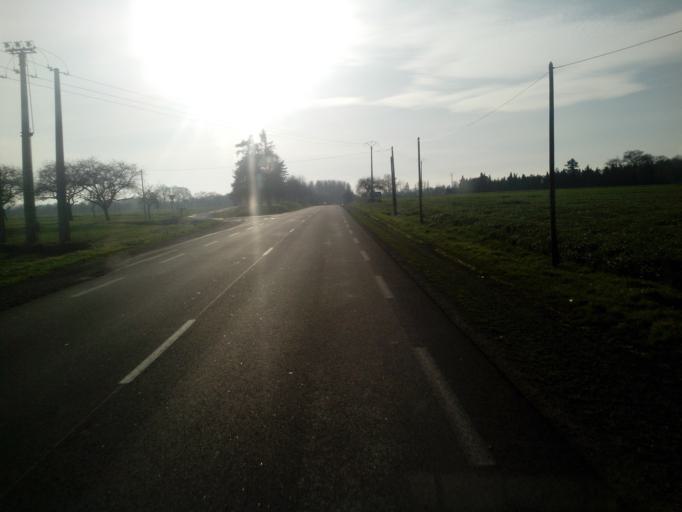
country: FR
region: Brittany
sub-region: Departement du Morbihan
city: Mauron
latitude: 48.1068
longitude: -2.2574
